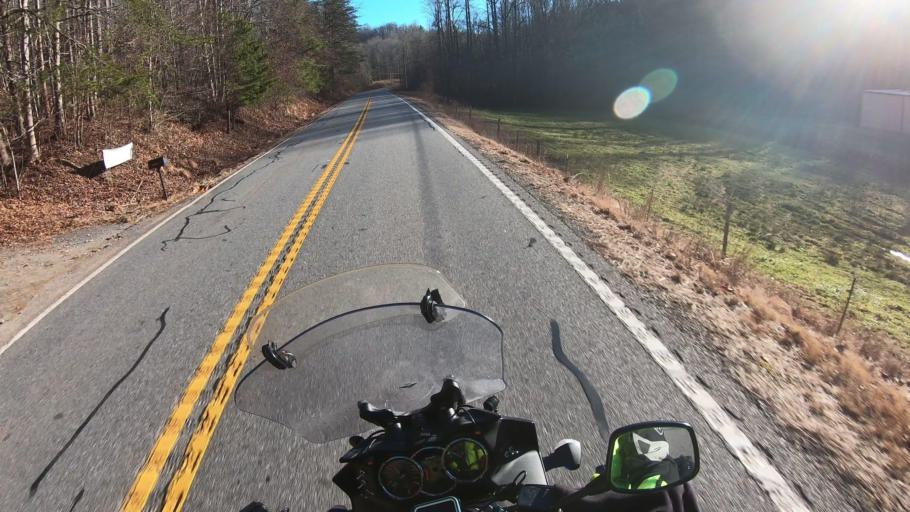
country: US
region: Georgia
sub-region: Fannin County
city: Blue Ridge
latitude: 34.8210
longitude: -84.1886
